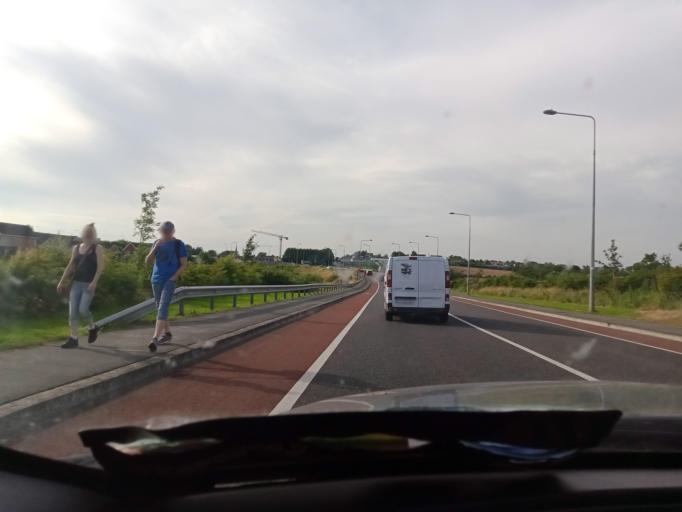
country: IE
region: Ulster
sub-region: An Cabhan
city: Cavan
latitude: 53.9882
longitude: -7.3517
